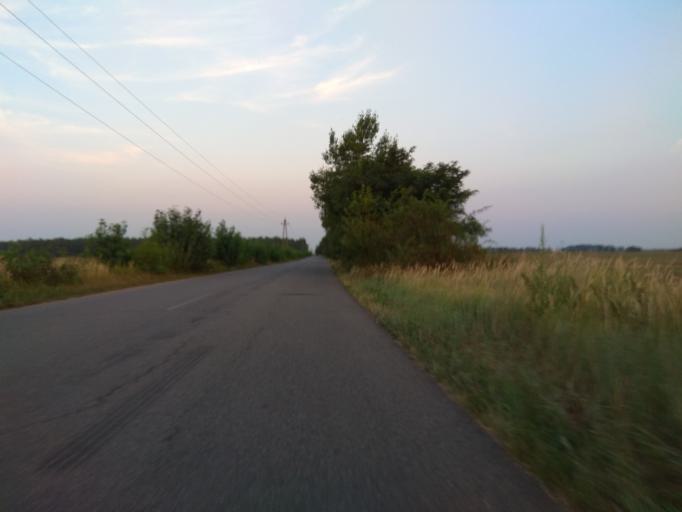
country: HU
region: Borsod-Abauj-Zemplen
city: Emod
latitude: 47.9124
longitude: 20.8508
